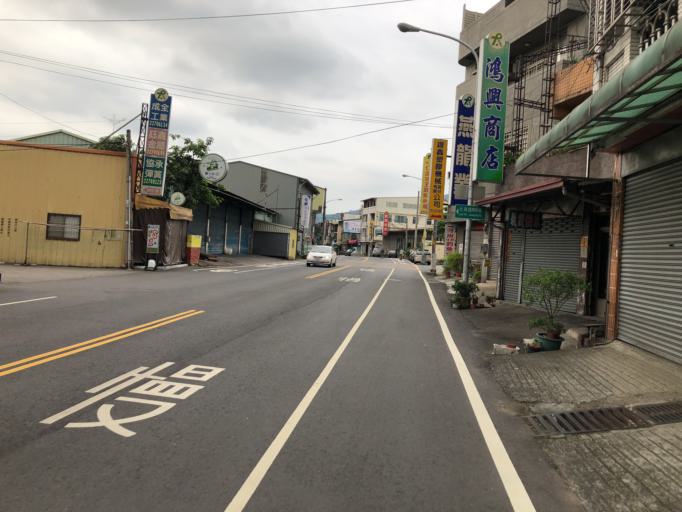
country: TW
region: Taiwan
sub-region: Taichung City
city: Taichung
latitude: 24.1131
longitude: 120.7316
